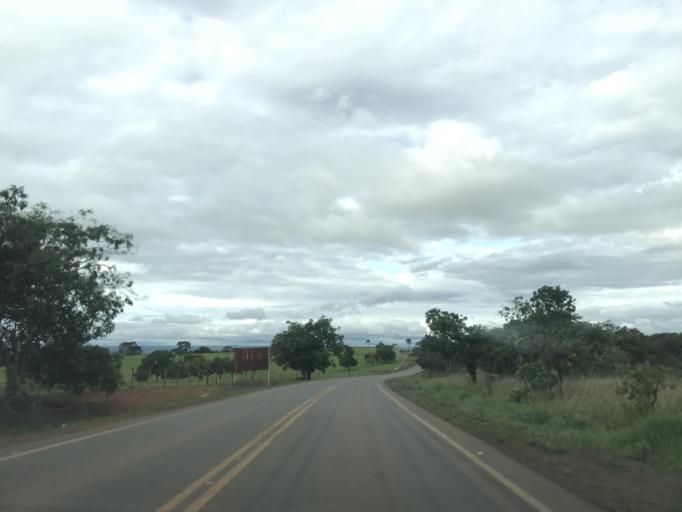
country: BR
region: Goias
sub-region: Vianopolis
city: Vianopolis
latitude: -16.7070
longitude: -48.3950
